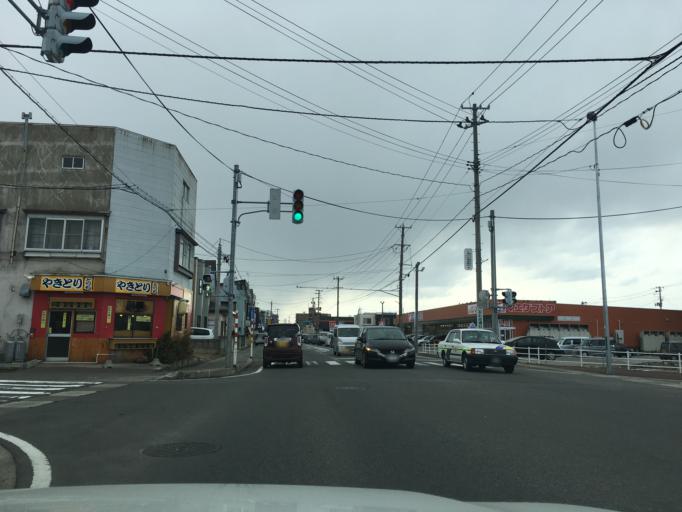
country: JP
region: Aomori
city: Aomori Shi
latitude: 40.8318
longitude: 140.7891
